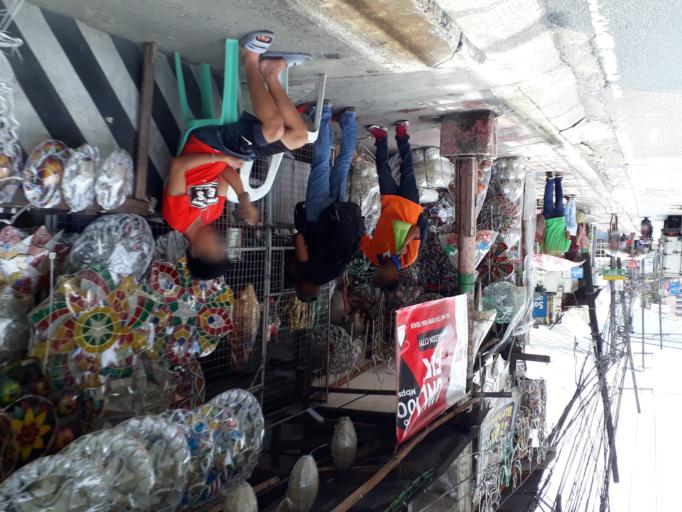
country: PH
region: Metro Manila
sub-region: San Juan
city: San Juan
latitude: 14.6097
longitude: 121.0373
